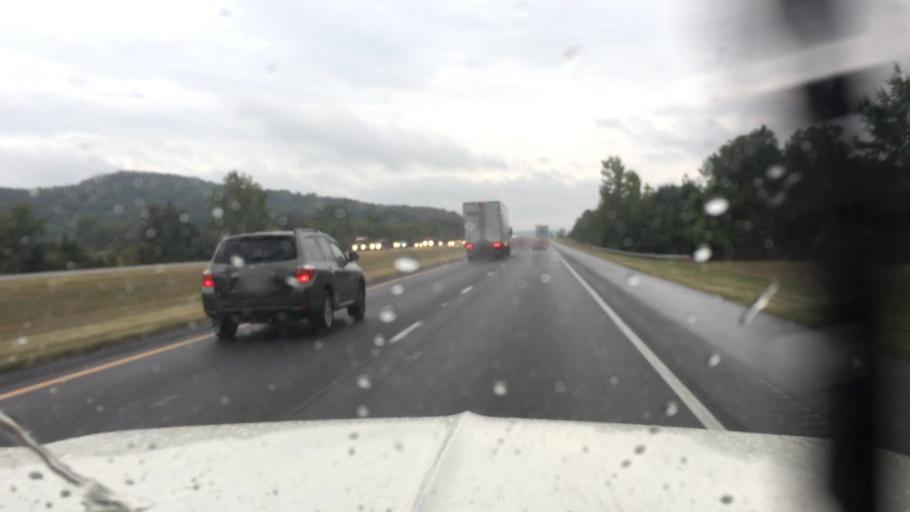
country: US
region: Alabama
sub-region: Morgan County
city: Falkville
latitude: 34.3950
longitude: -86.8964
